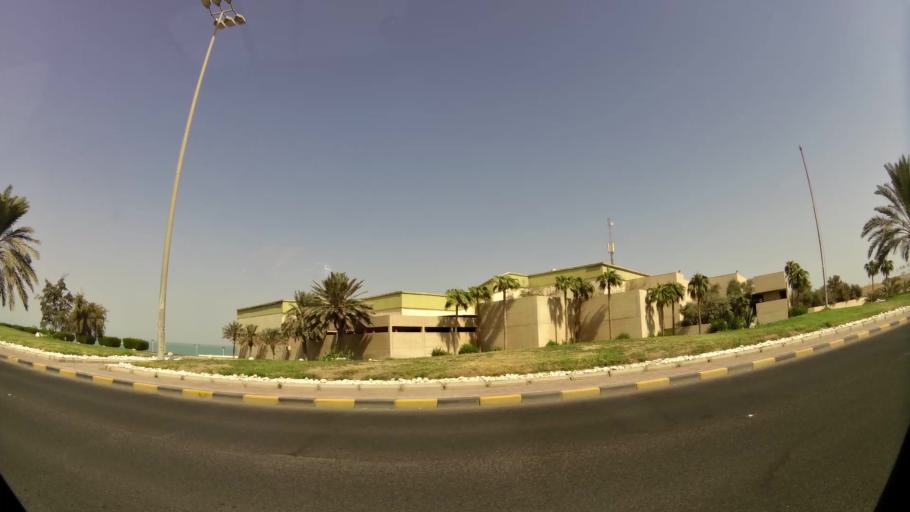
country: KW
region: Muhafazat Hawalli
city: Hawalli
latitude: 29.3445
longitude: 48.0434
